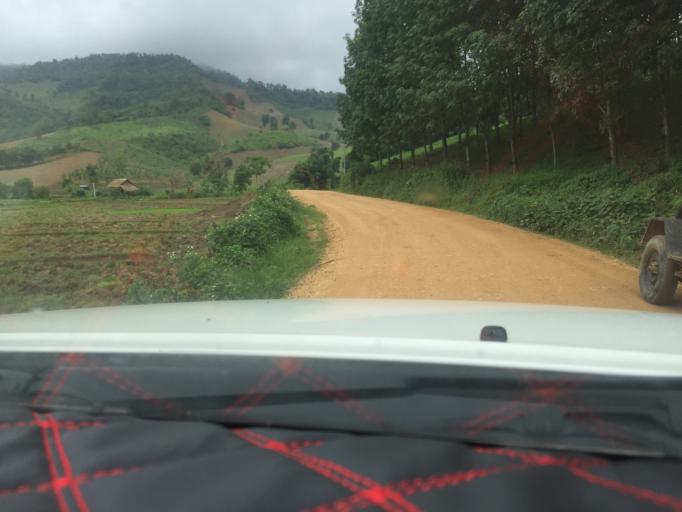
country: TH
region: Phayao
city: Phu Sang
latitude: 19.6952
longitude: 100.5001
